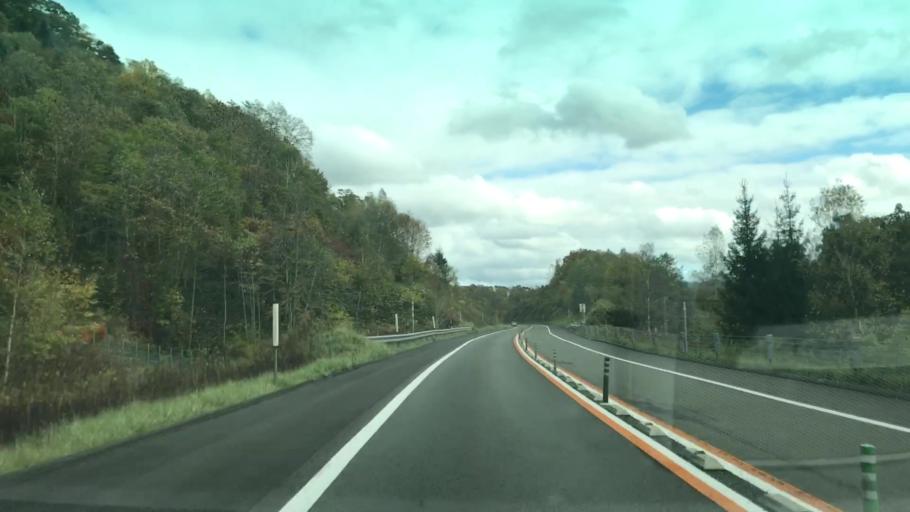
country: JP
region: Hokkaido
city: Chitose
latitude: 42.9175
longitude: 141.9597
